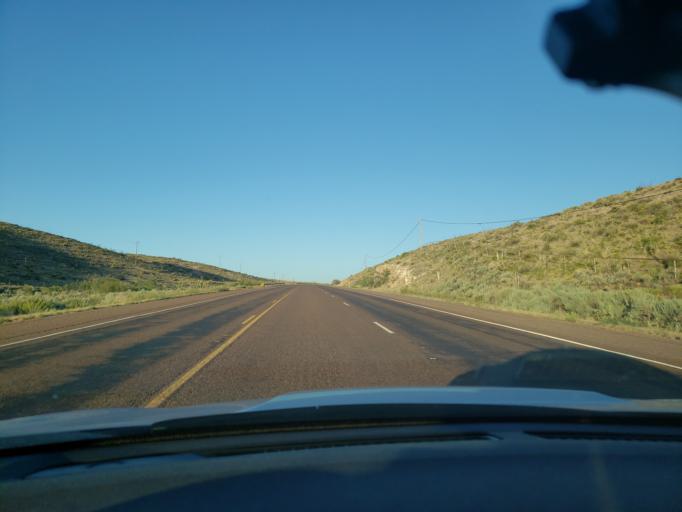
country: US
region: Texas
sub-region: El Paso County
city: Homestead Meadows South
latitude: 31.8272
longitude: -105.8935
